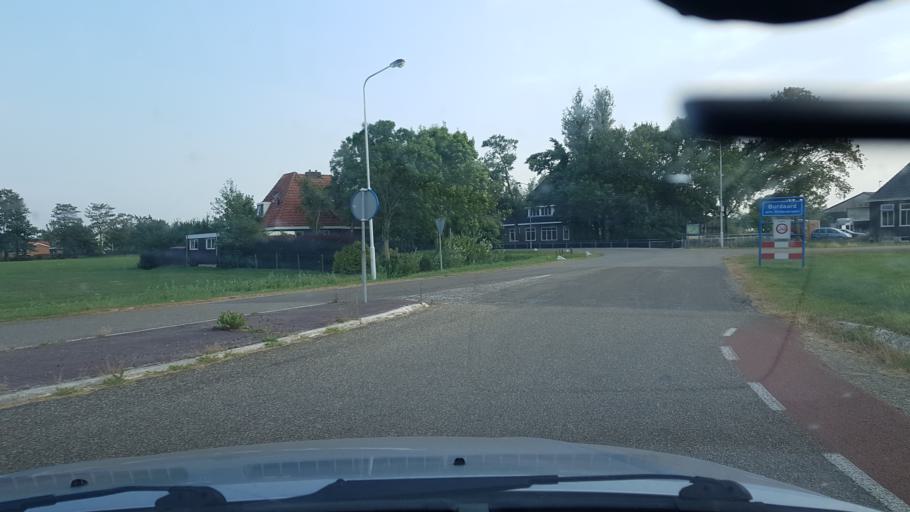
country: NL
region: Friesland
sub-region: Gemeente Ferwerderadiel
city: Burdaard
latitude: 53.2993
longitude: 5.8772
